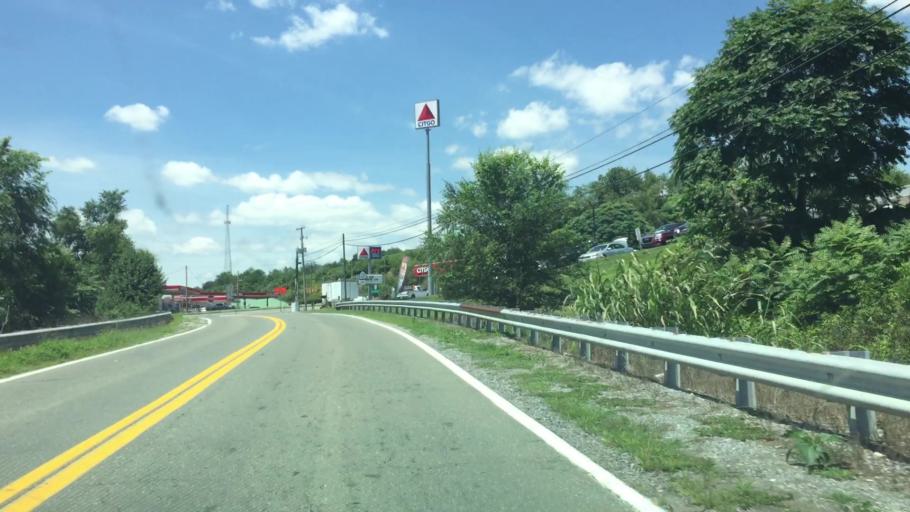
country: US
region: Virginia
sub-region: Wythe County
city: Wytheville
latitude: 36.9468
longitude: -80.9482
